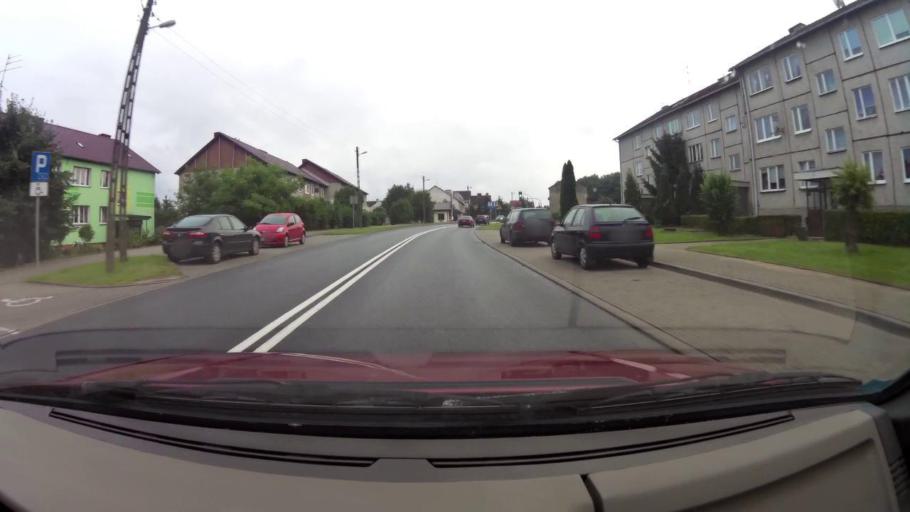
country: PL
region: West Pomeranian Voivodeship
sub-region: Powiat stargardzki
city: Chociwel
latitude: 53.4611
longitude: 15.3334
